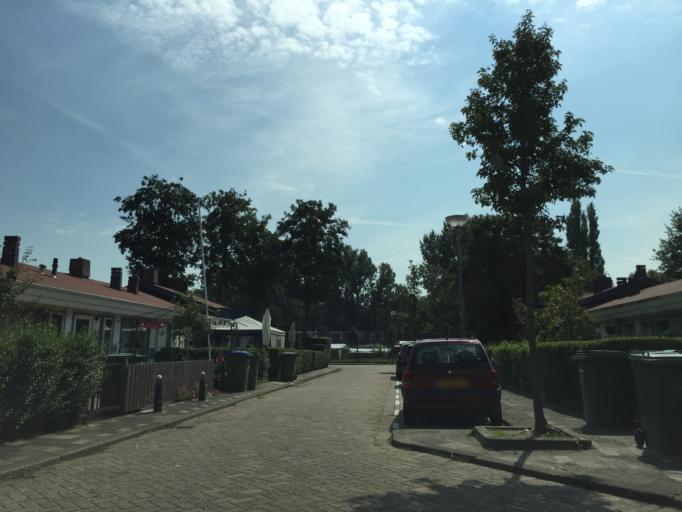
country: NL
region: South Holland
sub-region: Gemeente Rotterdam
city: Delfshaven
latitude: 51.9454
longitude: 4.4308
